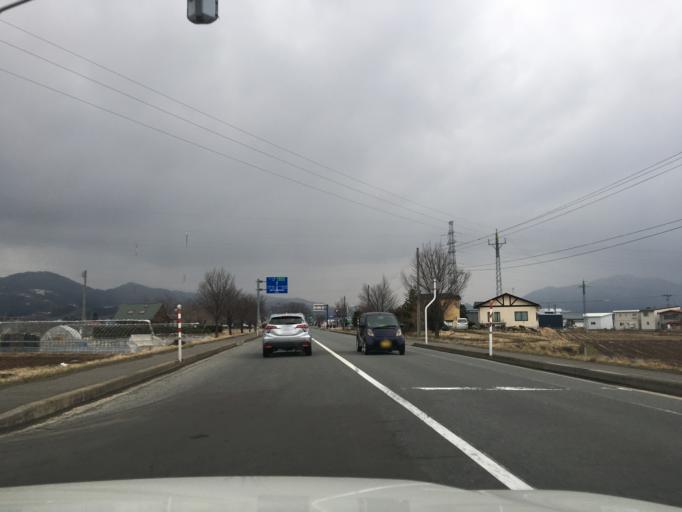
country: JP
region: Aomori
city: Kuroishi
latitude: 40.5754
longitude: 140.5683
